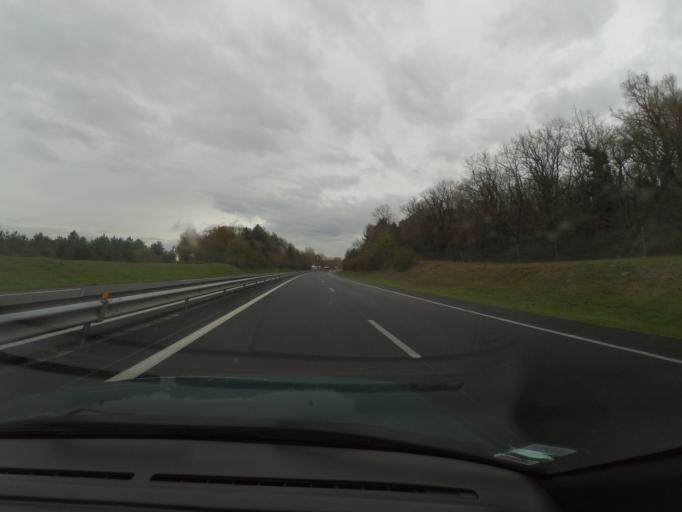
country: FR
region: Pays de la Loire
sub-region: Departement de Maine-et-Loire
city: Seiches-sur-le-Loir
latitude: 47.5748
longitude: -0.3351
